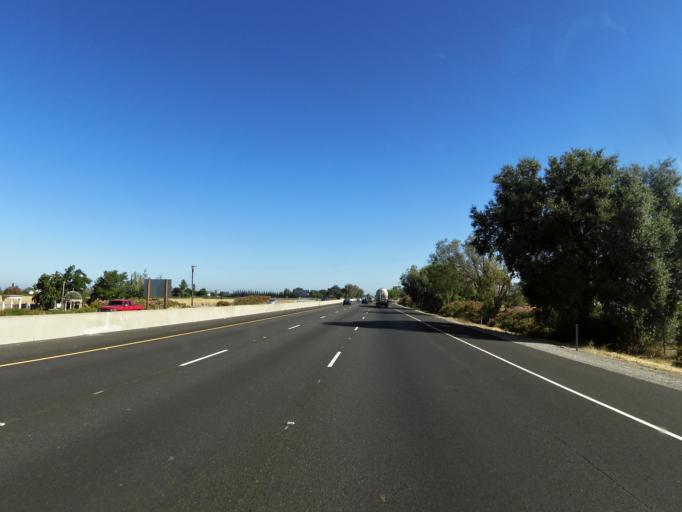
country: US
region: California
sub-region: San Joaquin County
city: Morada
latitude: 38.0586
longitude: -121.2594
